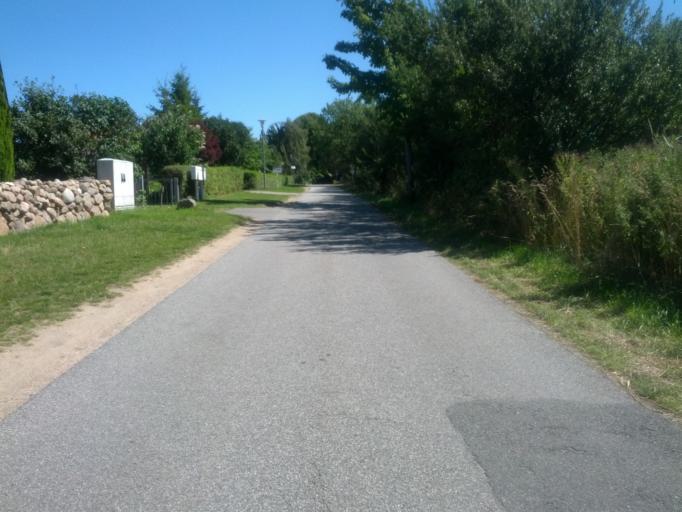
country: DE
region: Mecklenburg-Vorpommern
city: Bastorf
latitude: 54.1161
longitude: 11.6698
